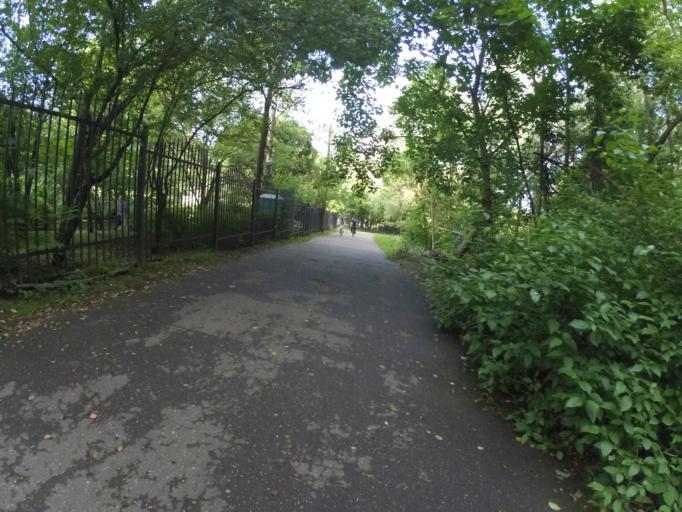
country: RU
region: Moscow
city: Ostankinskiy
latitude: 55.8439
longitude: 37.6142
